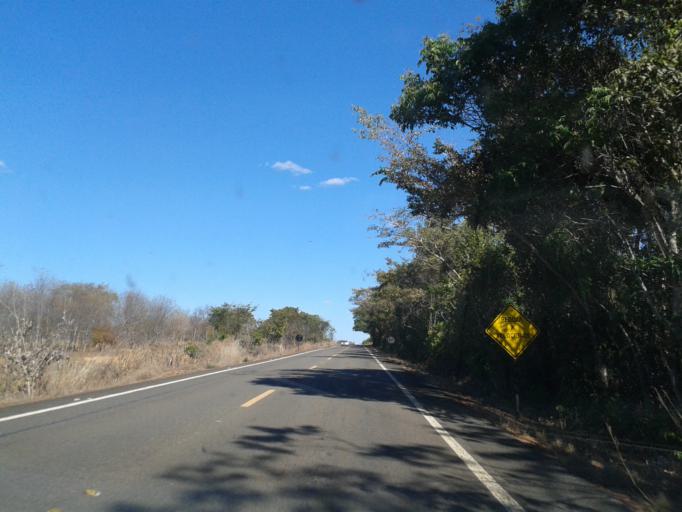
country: BR
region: Goias
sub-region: Sao Miguel Do Araguaia
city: Sao Miguel do Araguaia
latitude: -13.8856
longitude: -50.3295
